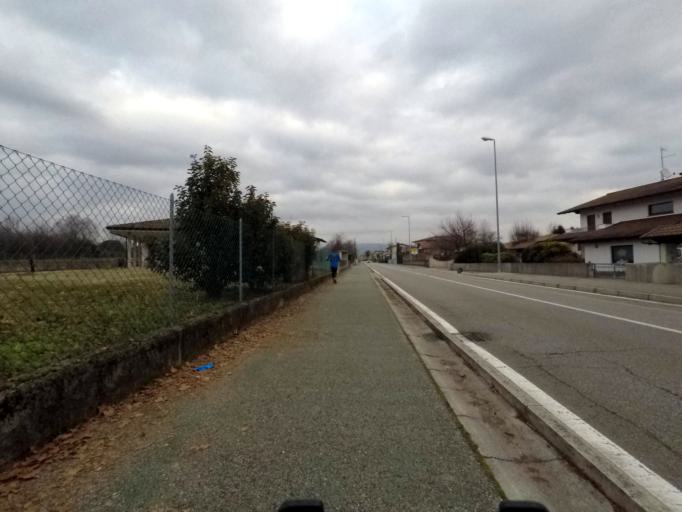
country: IT
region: Friuli Venezia Giulia
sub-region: Provincia di Udine
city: Tavagnacco
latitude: 46.1219
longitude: 13.2136
